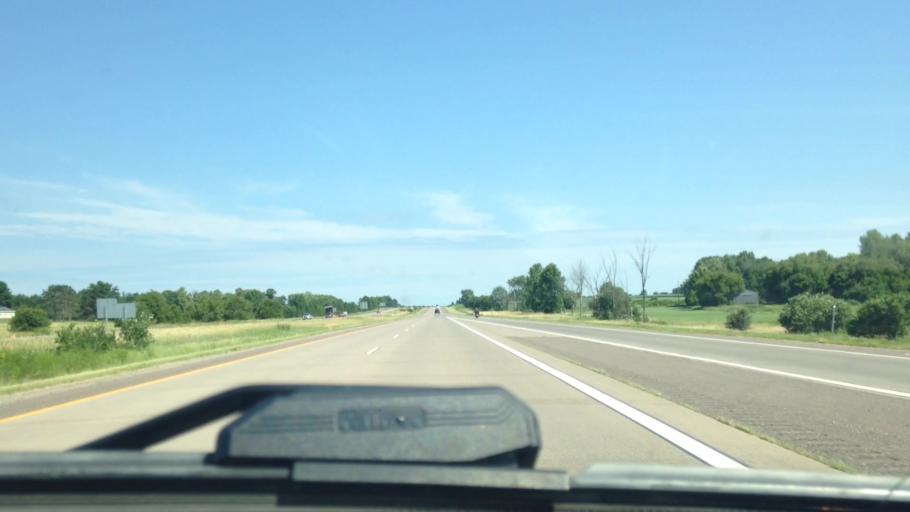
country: US
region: Wisconsin
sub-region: Barron County
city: Rice Lake
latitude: 45.4766
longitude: -91.7595
